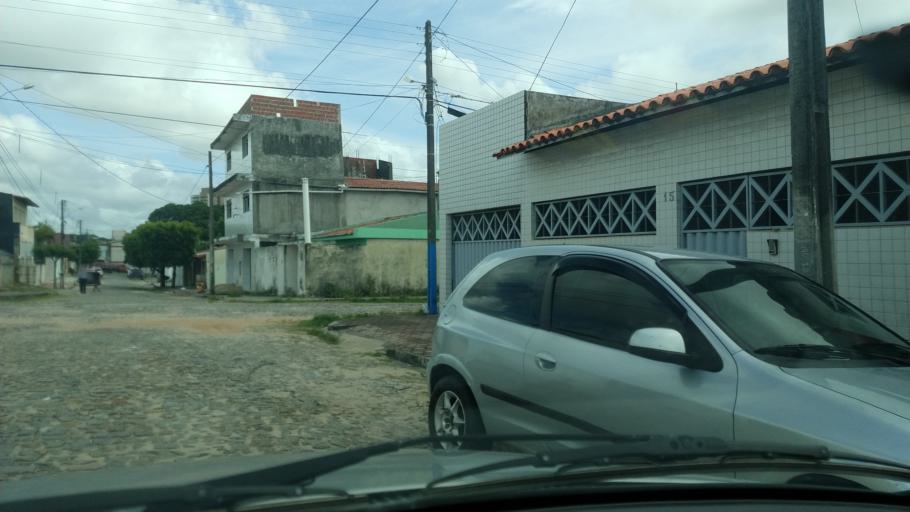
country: BR
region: Rio Grande do Norte
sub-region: Natal
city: Natal
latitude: -5.8643
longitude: -35.2059
